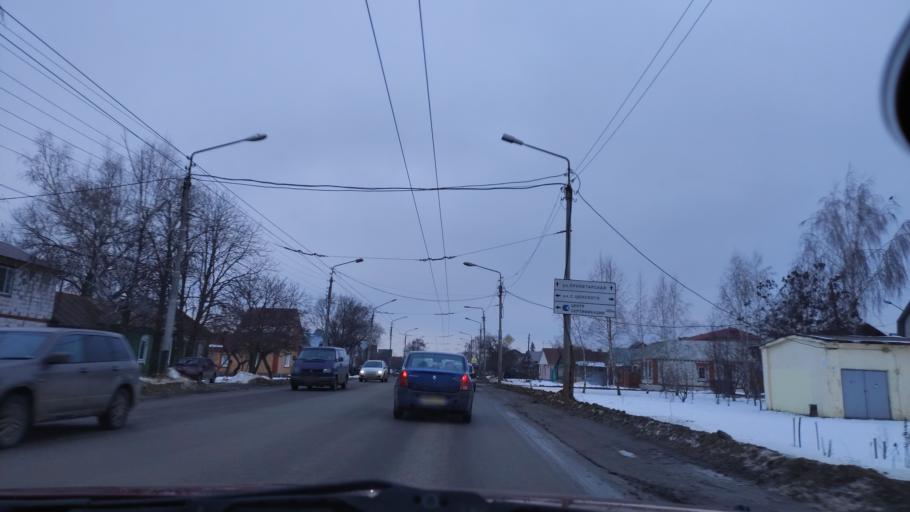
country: RU
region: Tambov
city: Tambov
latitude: 52.7050
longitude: 41.4544
